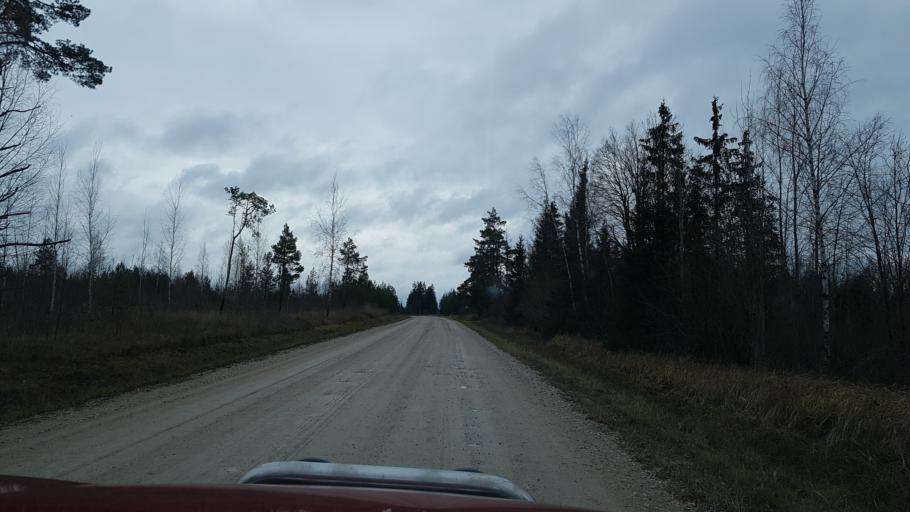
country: EE
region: Paernumaa
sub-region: Halinga vald
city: Parnu-Jaagupi
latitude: 58.5760
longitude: 24.4071
